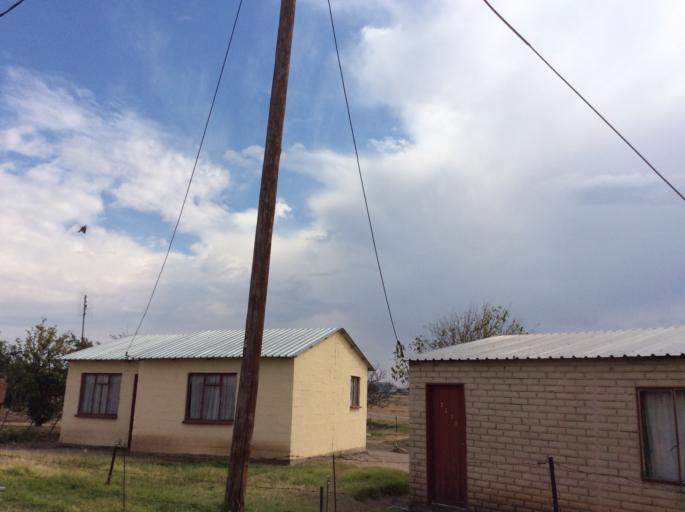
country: ZA
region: Orange Free State
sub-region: Xhariep District Municipality
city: Dewetsdorp
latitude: -29.5794
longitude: 26.6871
